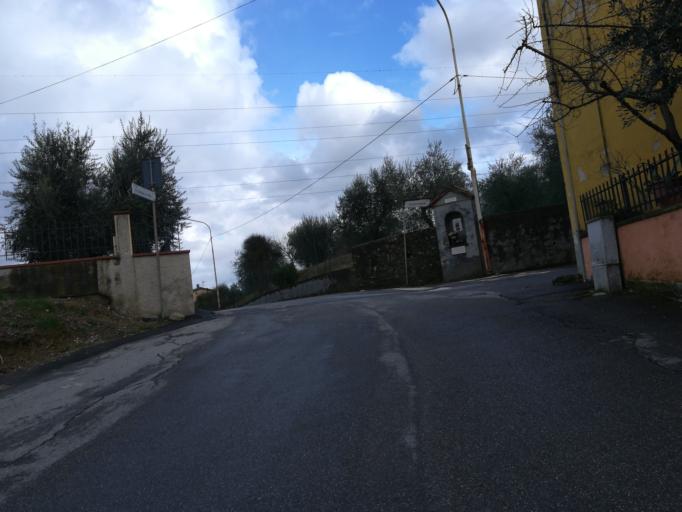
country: IT
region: Tuscany
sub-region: Provincia di Prato
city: Poggio A Caiano
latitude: 43.8076
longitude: 11.0515
